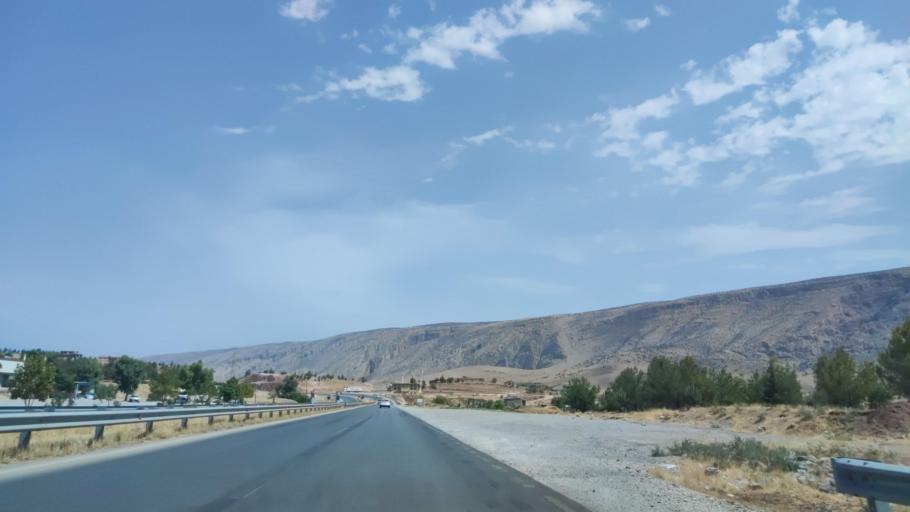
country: IQ
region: Arbil
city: Shaqlawah
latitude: 36.4817
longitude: 44.3810
